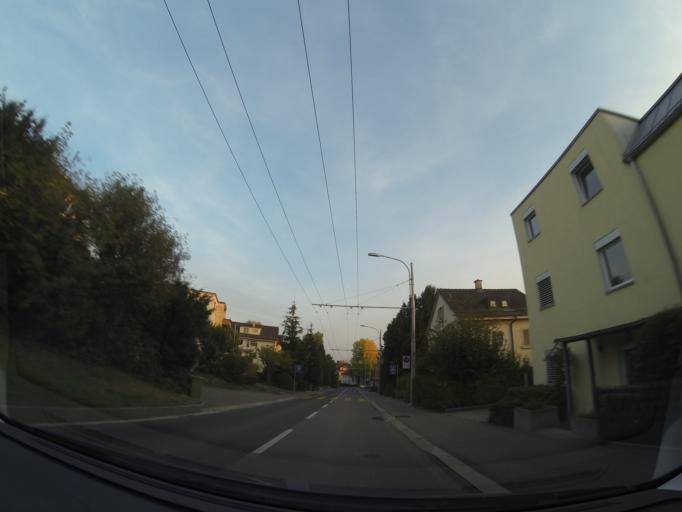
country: CH
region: Zurich
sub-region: Bezirk Zuerich
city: Zuerich (Kreis 10) / Hoengg
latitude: 47.4070
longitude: 8.4904
